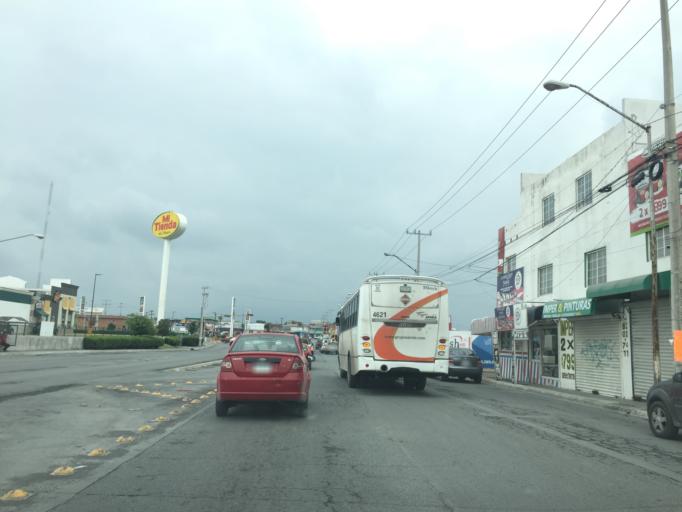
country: MX
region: Nuevo Leon
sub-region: Apodaca
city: Fraccionamiento Cosmopolis Octavo Sector
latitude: 25.7859
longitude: -100.2489
